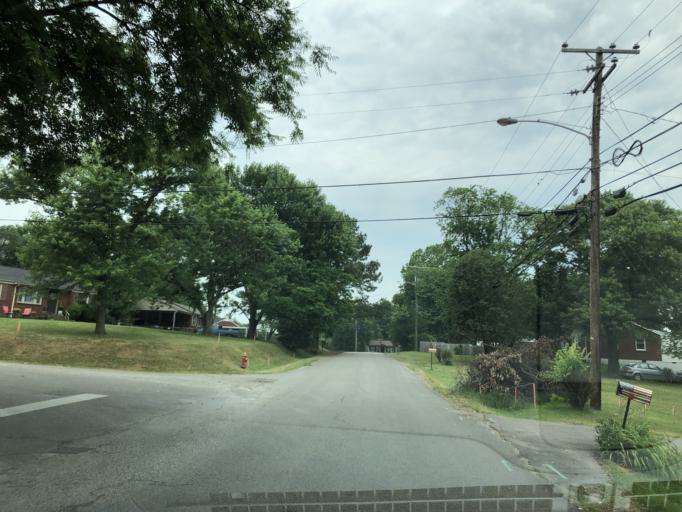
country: US
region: Tennessee
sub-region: Davidson County
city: Oak Hill
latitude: 36.0776
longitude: -86.6910
